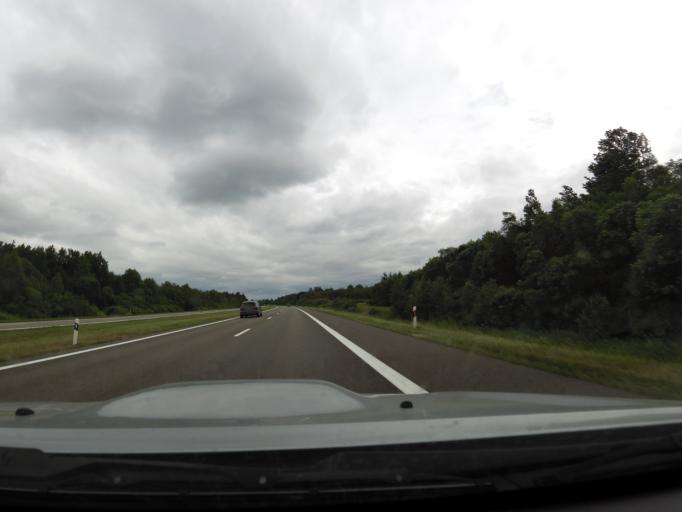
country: LT
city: Ramygala
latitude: 55.5822
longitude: 24.4605
